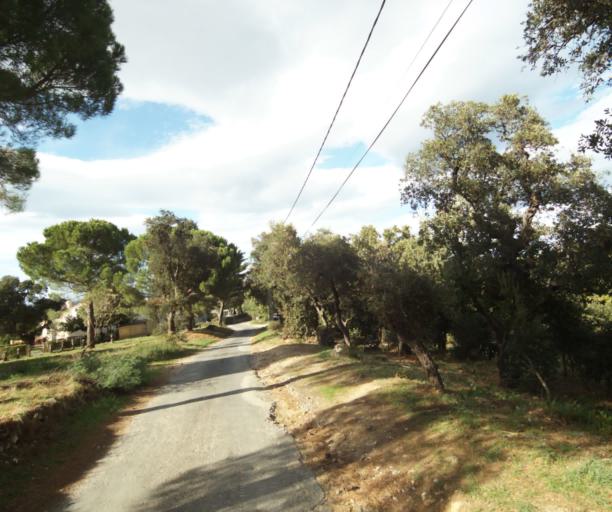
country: FR
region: Languedoc-Roussillon
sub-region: Departement des Pyrenees-Orientales
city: Argelers
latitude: 42.5303
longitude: 3.0263
